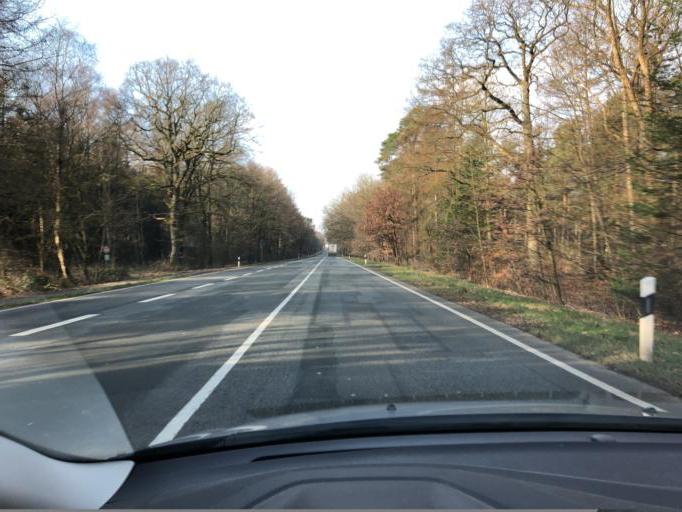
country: DE
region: Lower Saxony
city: Hesel
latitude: 53.3062
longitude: 7.6188
